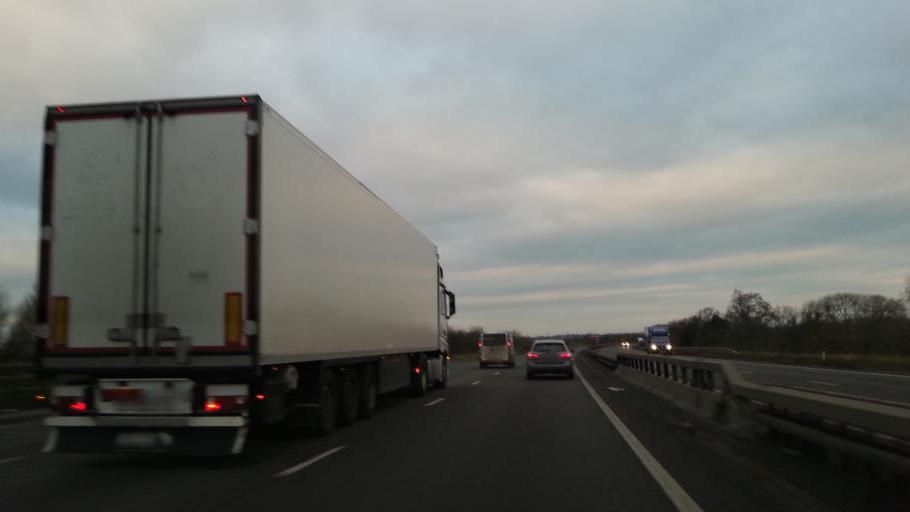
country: GB
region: England
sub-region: Nottinghamshire
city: Newark on Trent
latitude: 53.1052
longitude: -0.8063
